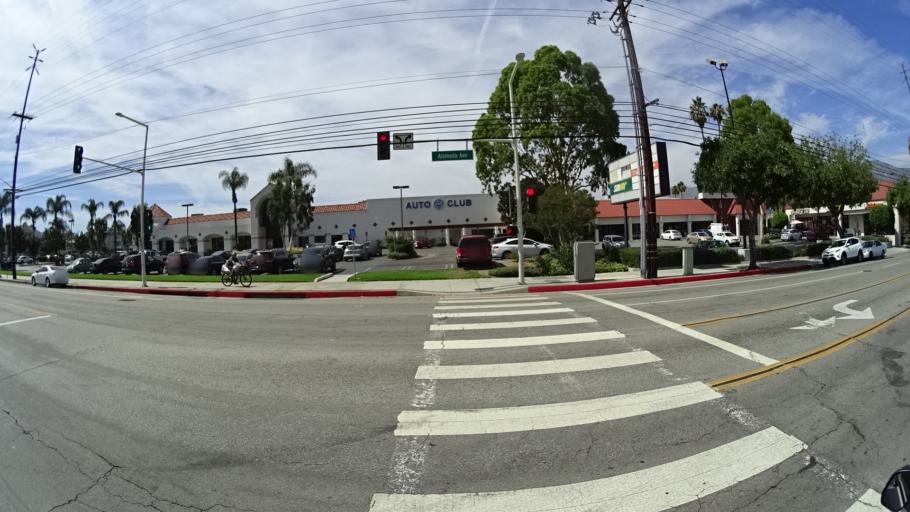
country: US
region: California
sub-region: Los Angeles County
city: Burbank
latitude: 34.1632
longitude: -118.3139
